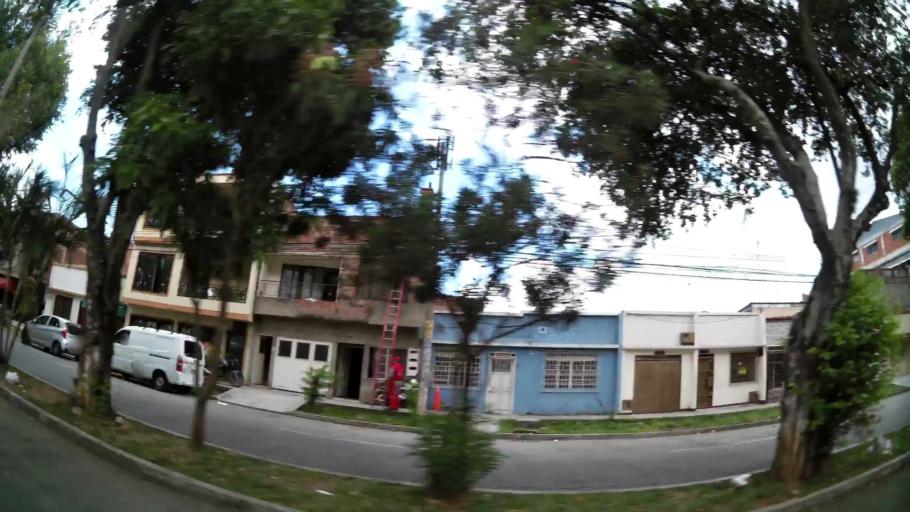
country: CO
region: Valle del Cauca
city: Cali
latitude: 3.4371
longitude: -76.5306
